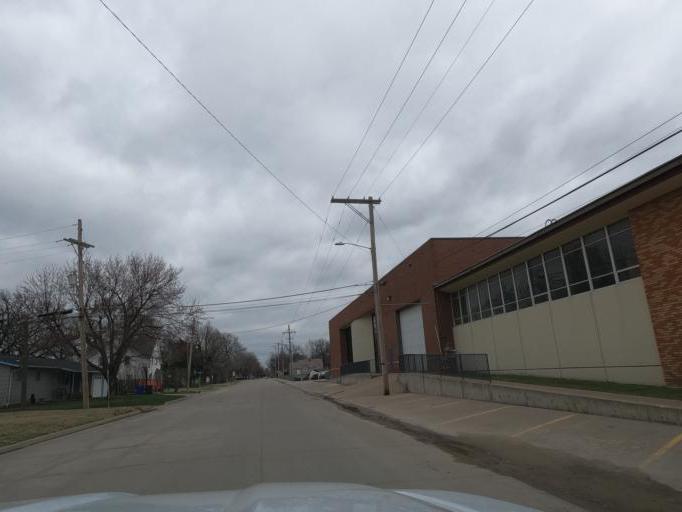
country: US
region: Kansas
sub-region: McPherson County
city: Inman
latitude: 38.2284
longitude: -97.7754
